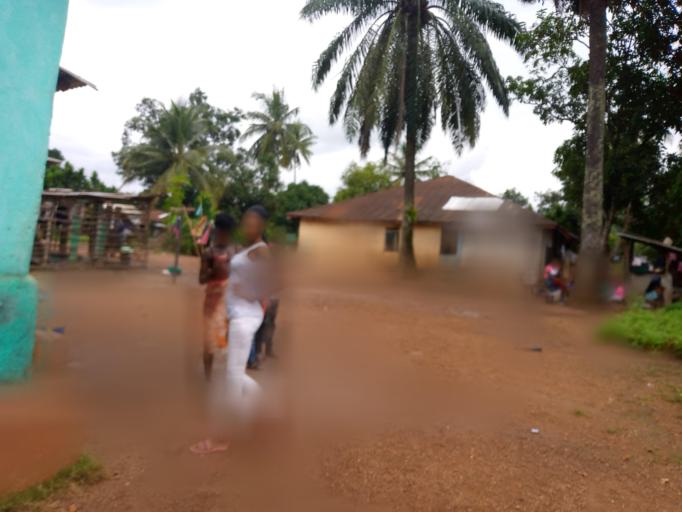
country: SL
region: Eastern Province
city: Kenema
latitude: 7.8708
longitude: -11.1858
